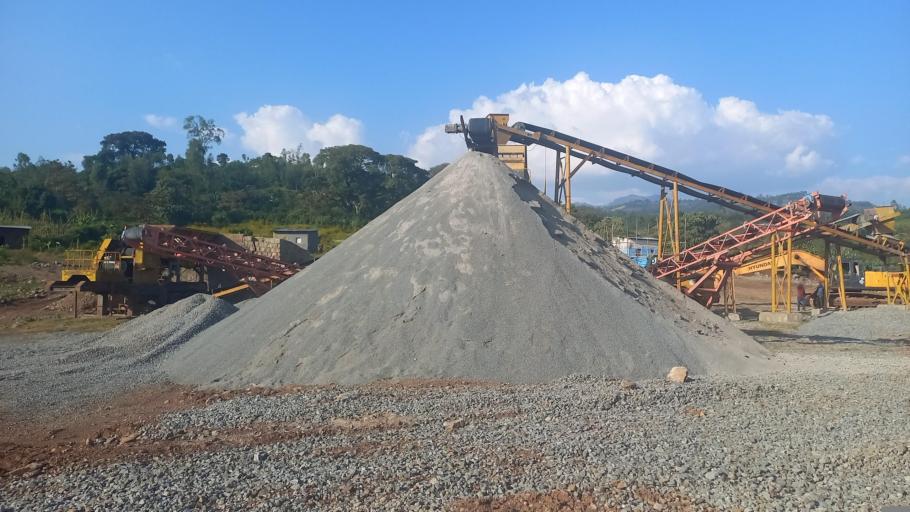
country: ET
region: Southern Nations, Nationalities, and People's Region
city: Areka
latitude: 7.2284
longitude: 37.5929
